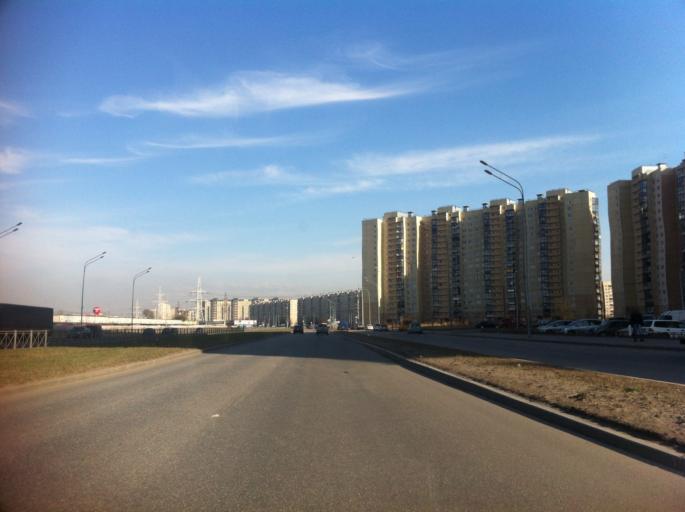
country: RU
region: St.-Petersburg
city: Uritsk
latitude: 59.8619
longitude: 30.1977
